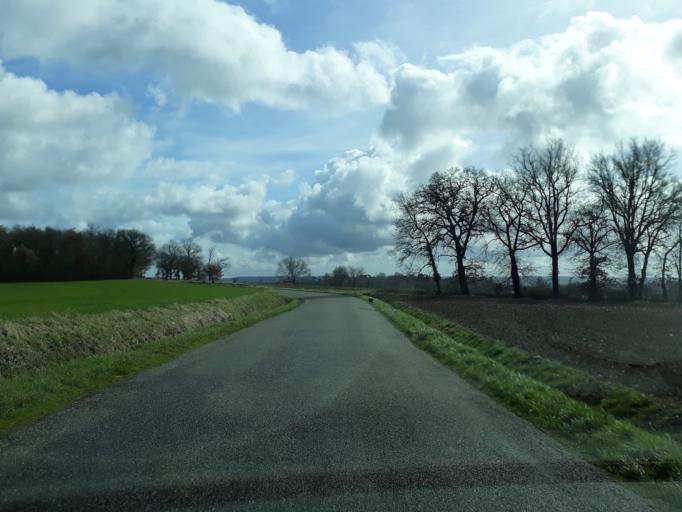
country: FR
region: Midi-Pyrenees
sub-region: Departement du Gers
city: Pujaudran
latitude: 43.6288
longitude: 1.0186
